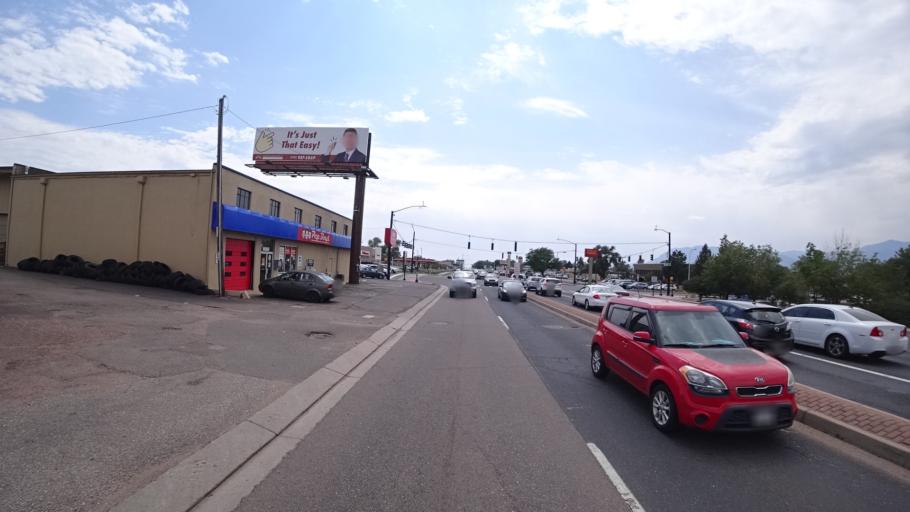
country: US
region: Colorado
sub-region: El Paso County
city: Colorado Springs
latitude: 38.8404
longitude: -104.7758
